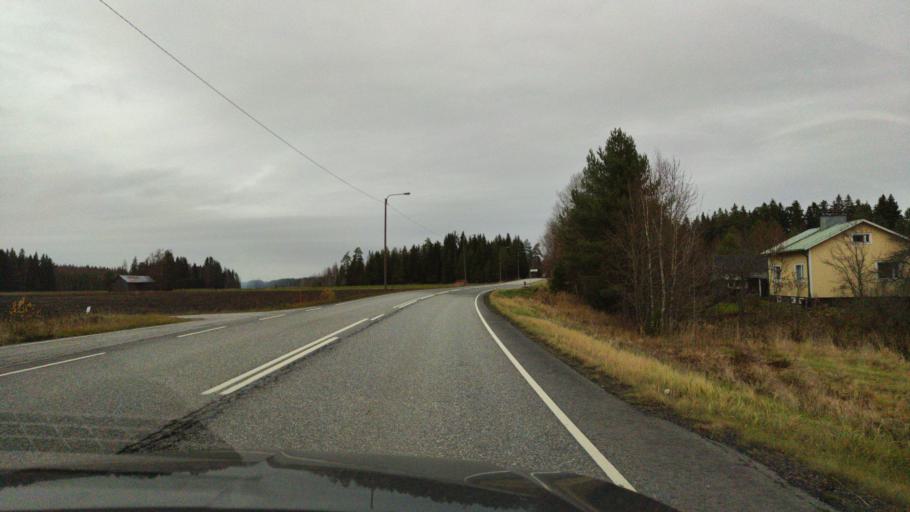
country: FI
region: Varsinais-Suomi
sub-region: Turku
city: Vahto
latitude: 60.6382
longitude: 22.4195
